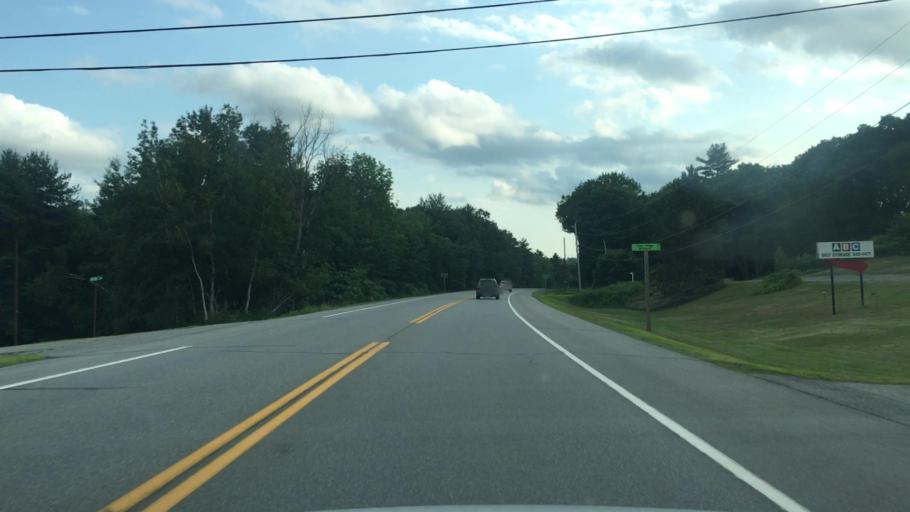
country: US
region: Maine
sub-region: Kennebec County
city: Windsor
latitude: 44.3648
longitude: -69.6345
